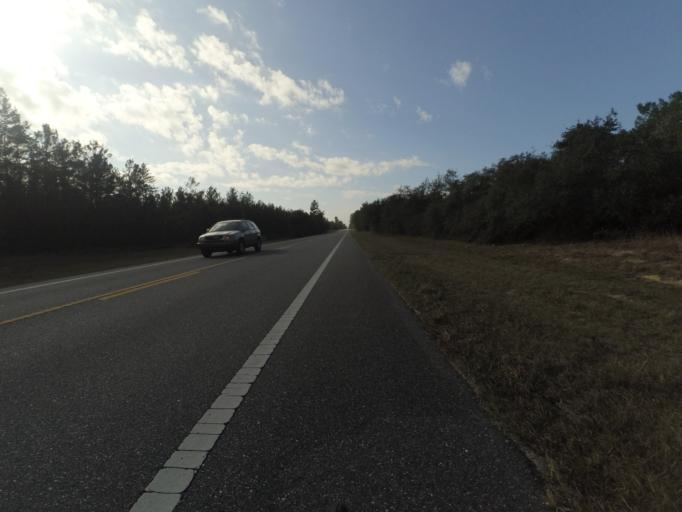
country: US
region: Florida
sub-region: Lake County
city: Astor
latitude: 29.0875
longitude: -81.6247
